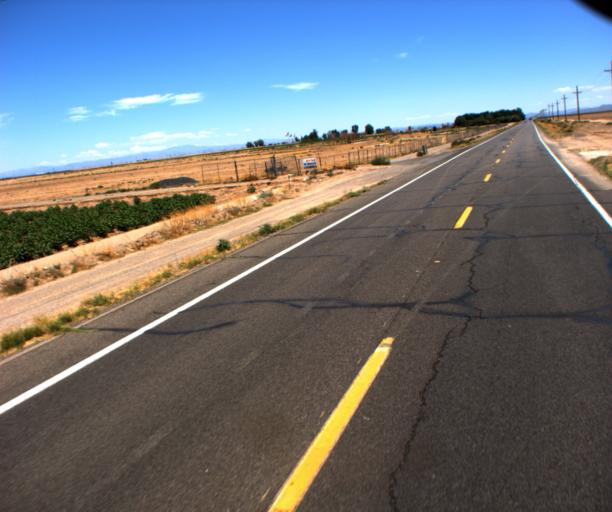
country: US
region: Arizona
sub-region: Pinal County
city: Casa Grande
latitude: 32.8798
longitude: -111.6371
